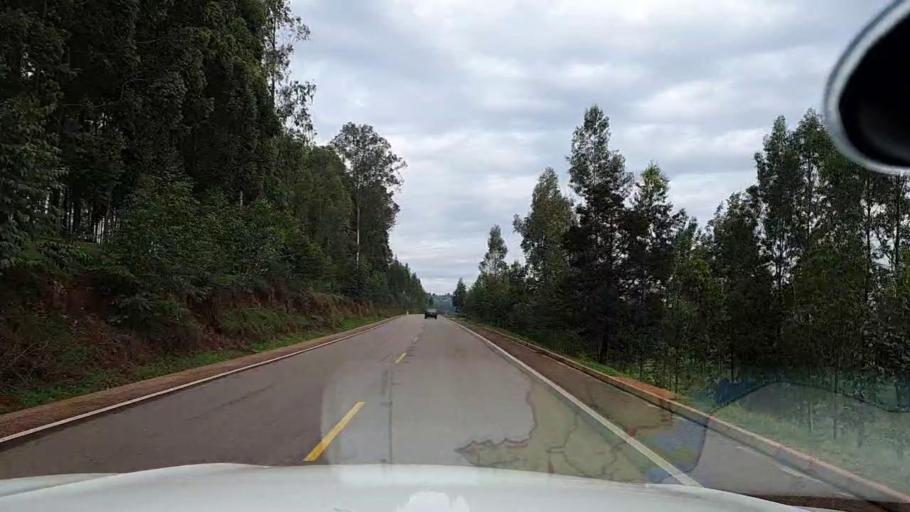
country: RW
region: Southern Province
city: Butare
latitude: -2.5613
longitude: 29.7205
